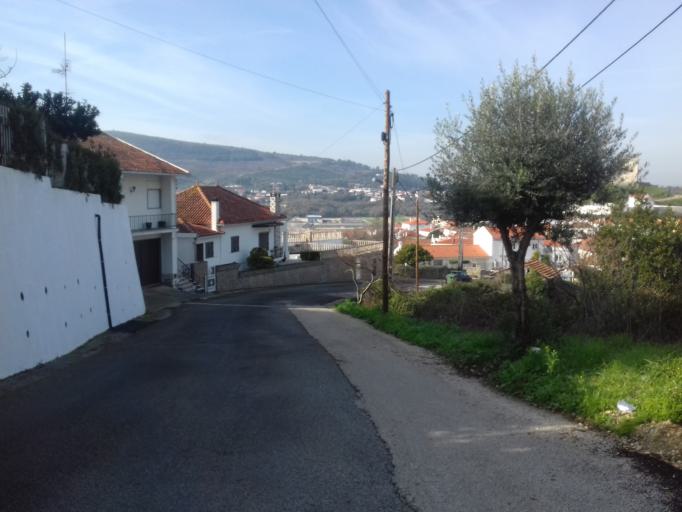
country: PT
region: Leiria
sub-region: Porto de Mos
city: Porto de Mos
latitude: 39.6029
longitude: -8.8141
